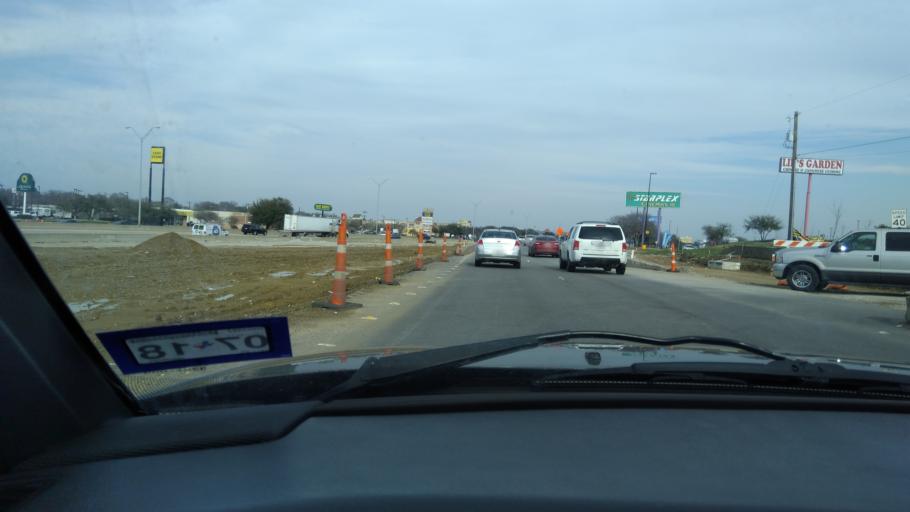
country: US
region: Texas
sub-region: Dallas County
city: Irving
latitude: 32.8363
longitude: -97.0088
